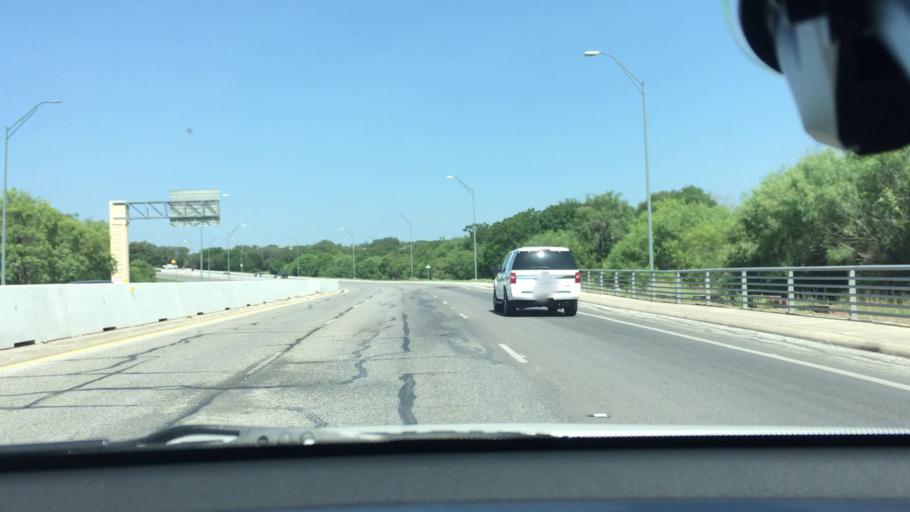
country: US
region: Texas
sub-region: Bexar County
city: Shavano Park
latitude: 29.5596
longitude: -98.5279
